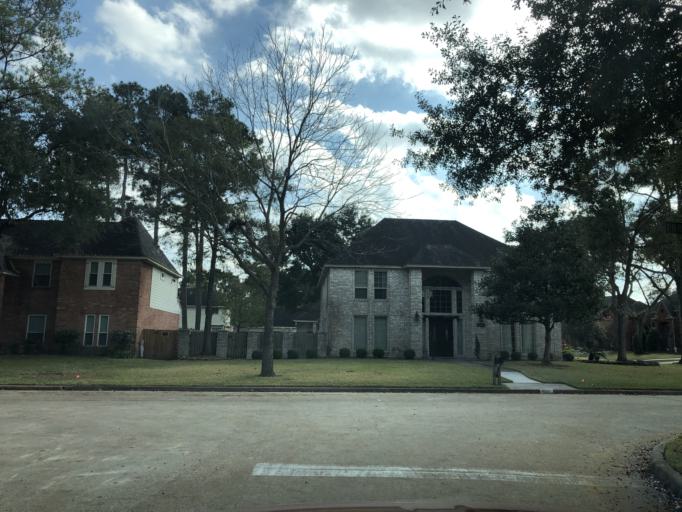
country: US
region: Texas
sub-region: Harris County
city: Tomball
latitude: 30.0257
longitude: -95.5439
